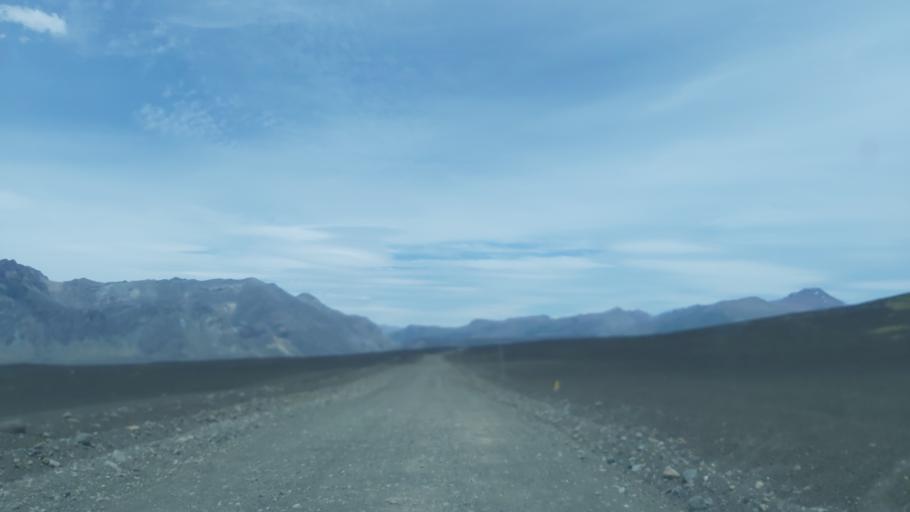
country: AR
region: Neuquen
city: Andacollo
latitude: -37.4254
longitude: -71.2873
